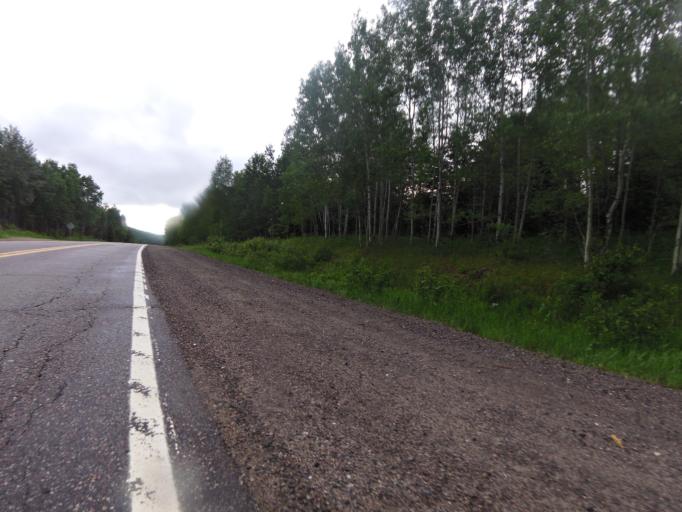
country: CA
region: Quebec
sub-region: Outaouais
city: Shawville
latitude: 45.9071
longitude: -76.2900
